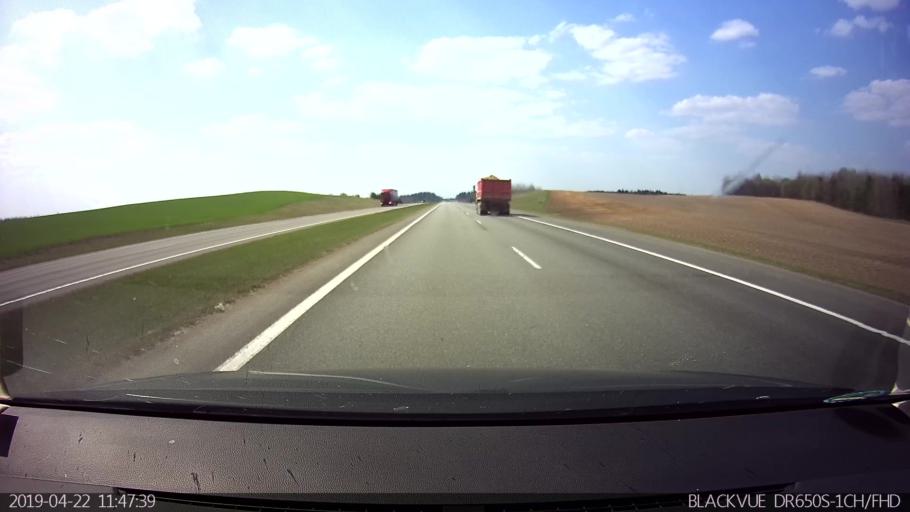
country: BY
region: Minsk
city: Horad Smalyavichy
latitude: 53.9818
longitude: 28.0760
